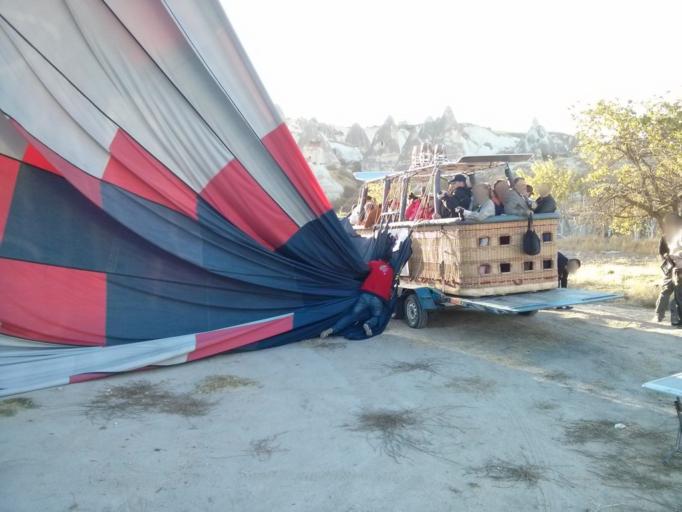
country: TR
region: Nevsehir
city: Goereme
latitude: 38.6425
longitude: 34.8379
